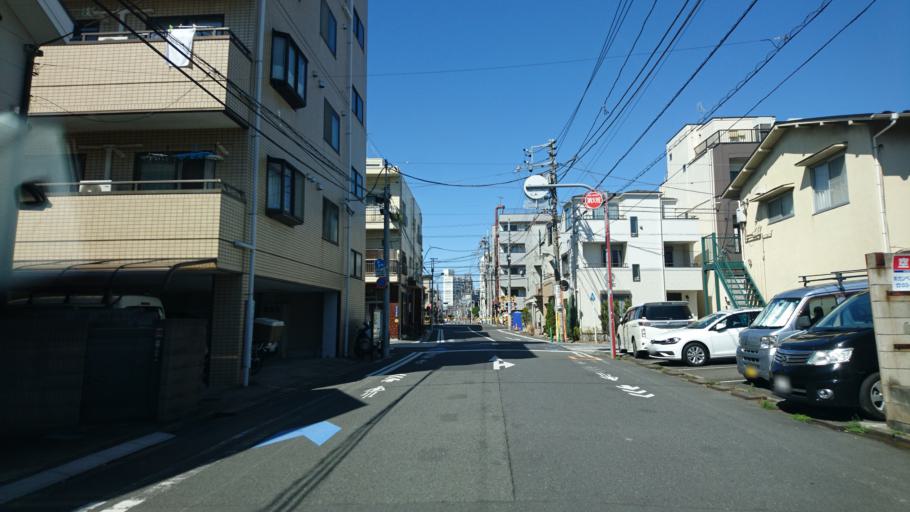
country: JP
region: Kanagawa
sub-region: Kawasaki-shi
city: Kawasaki
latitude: 35.5714
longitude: 139.7005
